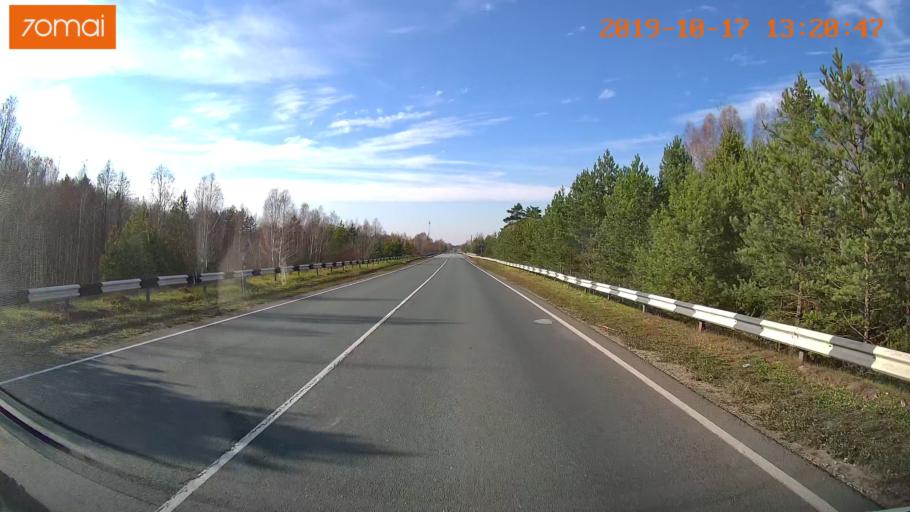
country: RU
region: Rjazan
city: Gus'-Zheleznyy
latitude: 55.0784
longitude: 41.0429
